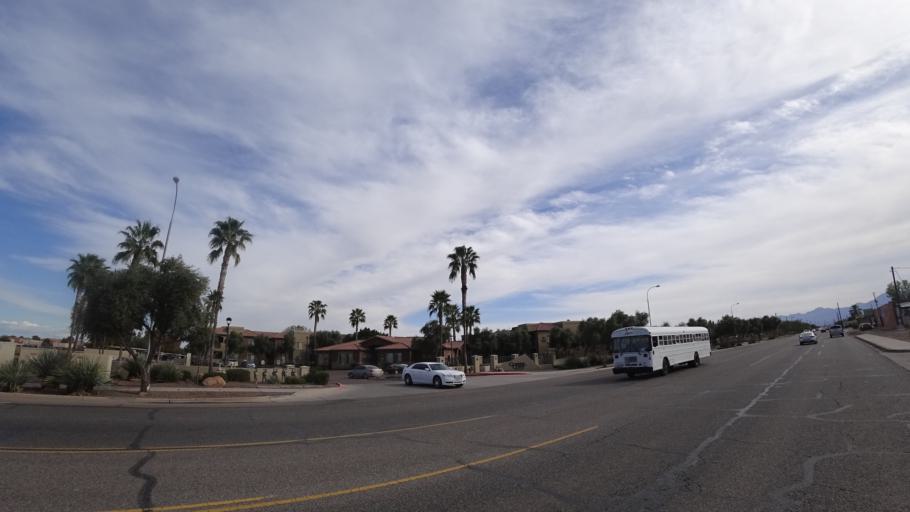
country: US
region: Arizona
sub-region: Maricopa County
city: Tolleson
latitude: 33.4486
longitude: -112.2552
